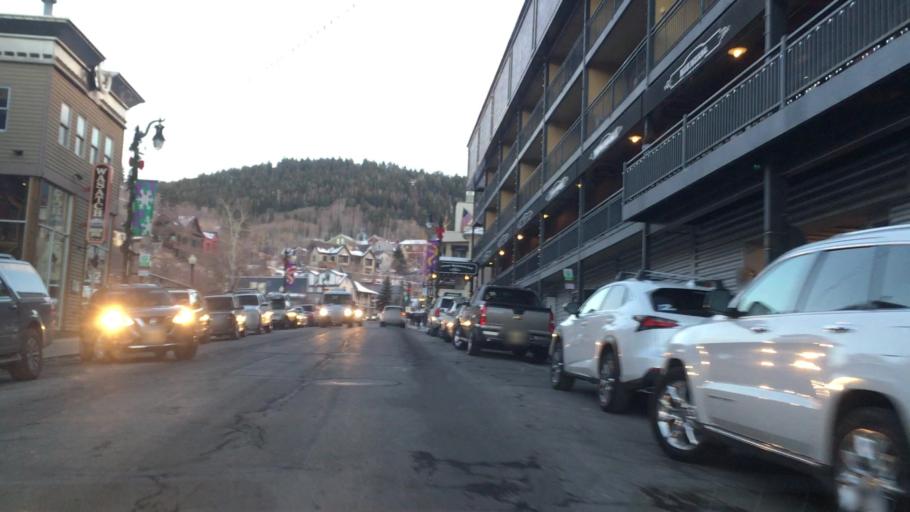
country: US
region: Utah
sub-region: Summit County
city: Park City
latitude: 40.6420
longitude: -111.4949
